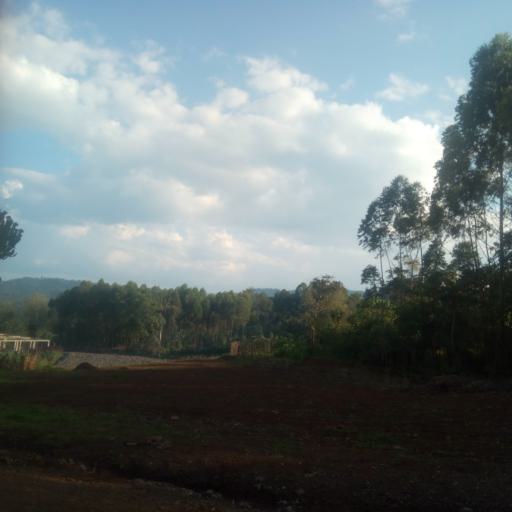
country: ET
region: Oromiya
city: Gore
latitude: 7.8366
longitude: 35.4708
